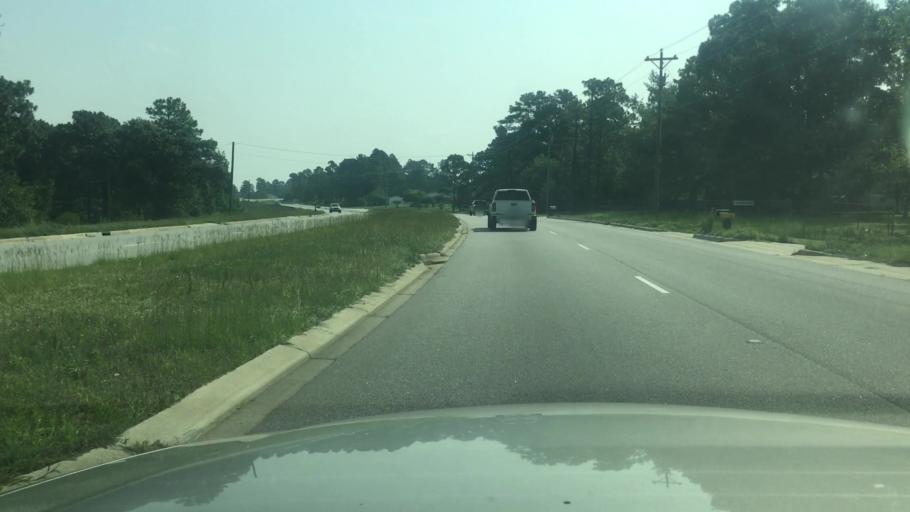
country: US
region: North Carolina
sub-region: Cumberland County
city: Hope Mills
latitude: 34.9925
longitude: -78.9453
